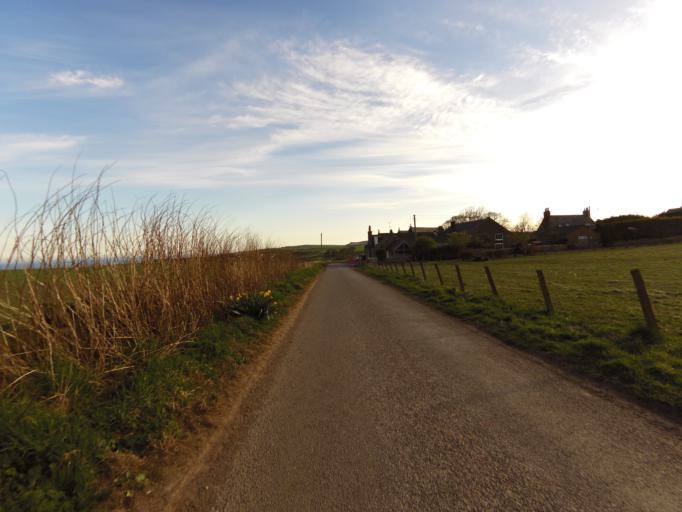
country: GB
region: Scotland
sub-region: Aberdeenshire
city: Stonehaven
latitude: 56.9017
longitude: -2.2161
